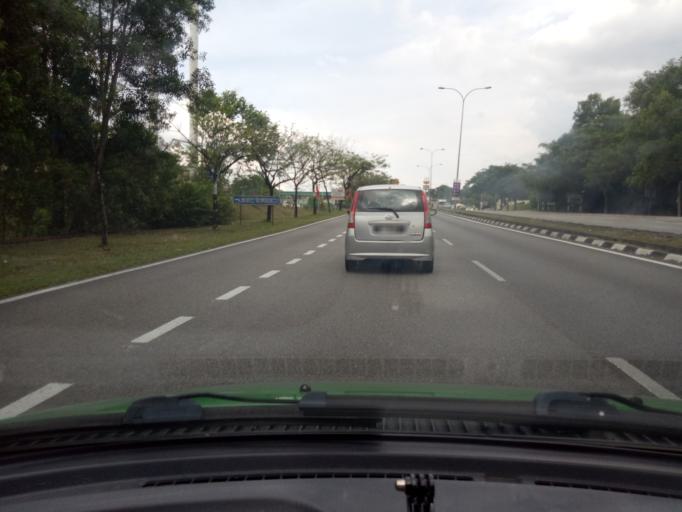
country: MY
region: Selangor
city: Kampong Baharu Balakong
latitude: 3.0087
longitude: 101.8017
